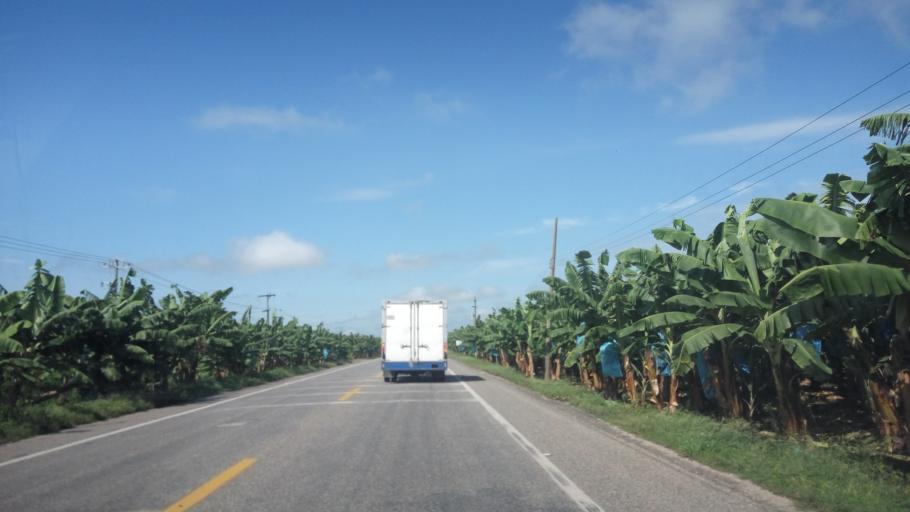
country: MX
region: Tabasco
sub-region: Teapa
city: Eureka y Belen
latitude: 17.6535
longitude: -92.9592
